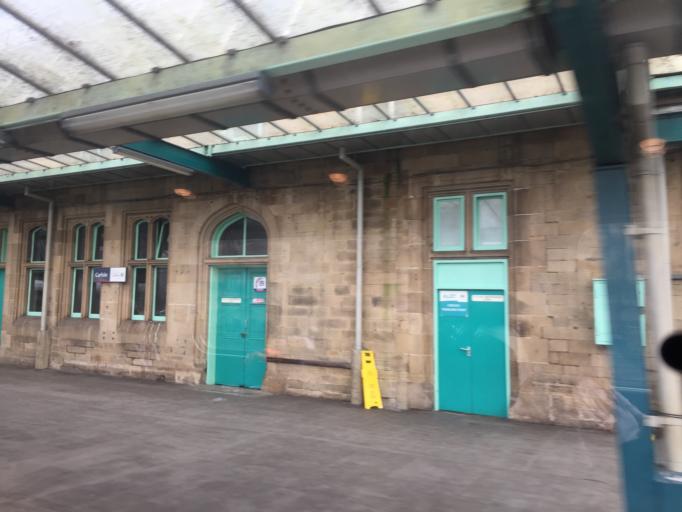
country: GB
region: England
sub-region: Cumbria
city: Carlisle
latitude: 54.8899
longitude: -2.9324
